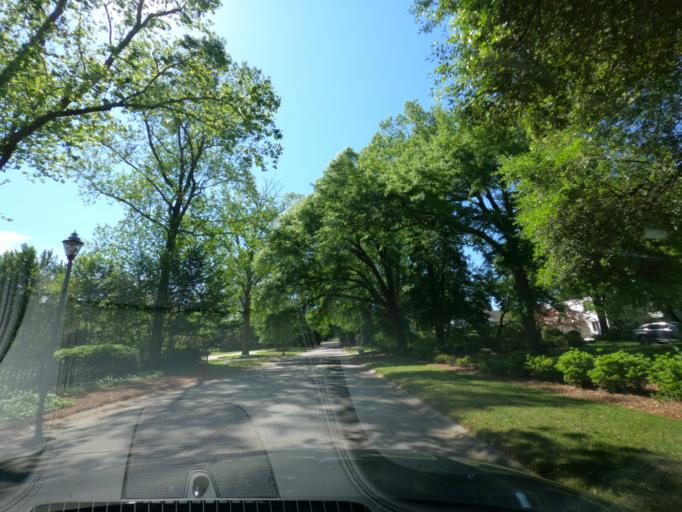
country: US
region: Georgia
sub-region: Columbia County
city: Martinez
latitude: 33.4727
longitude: -82.0432
